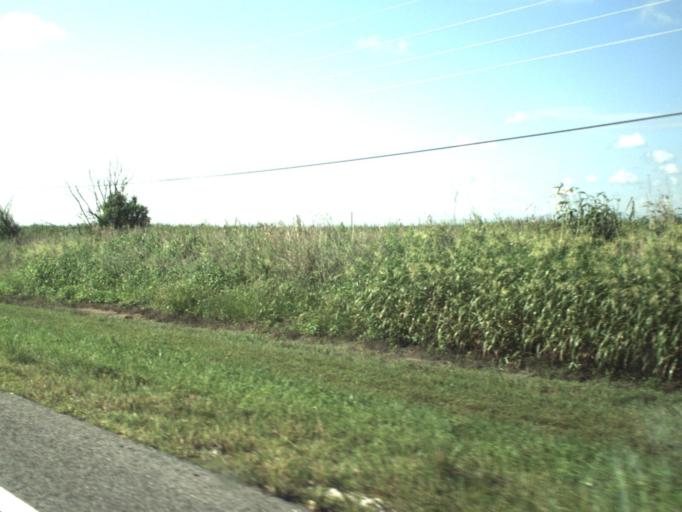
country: US
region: Florida
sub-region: Broward County
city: Coral Springs
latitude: 26.3494
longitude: -80.5493
